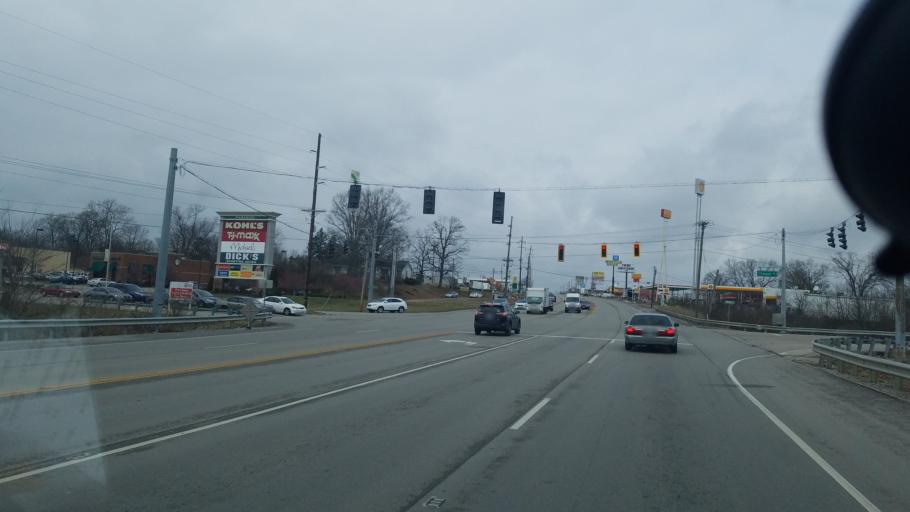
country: US
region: Kentucky
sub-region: Franklin County
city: Frankfort
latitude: 38.1761
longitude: -84.8124
